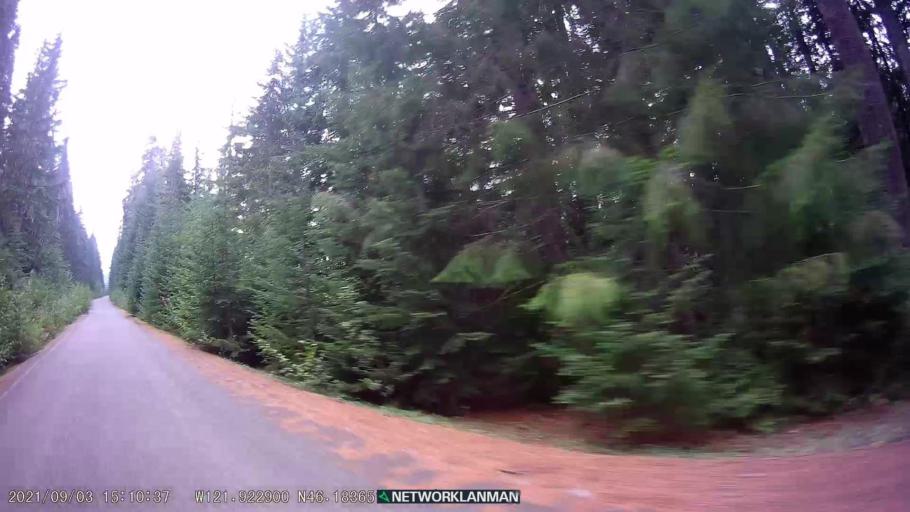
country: US
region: Washington
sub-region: Skamania County
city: Carson
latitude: 46.1834
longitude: -121.9231
